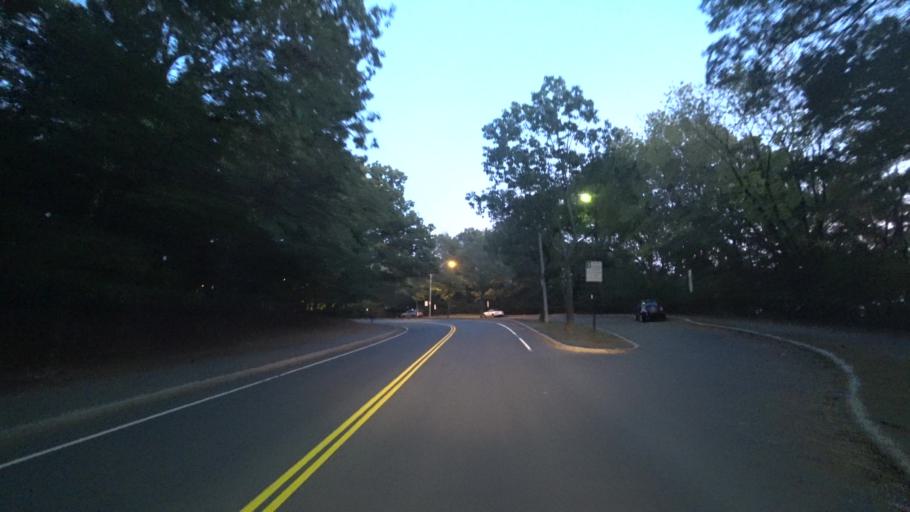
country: US
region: Massachusetts
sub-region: Norfolk County
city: Brookline
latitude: 42.3378
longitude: -71.1605
